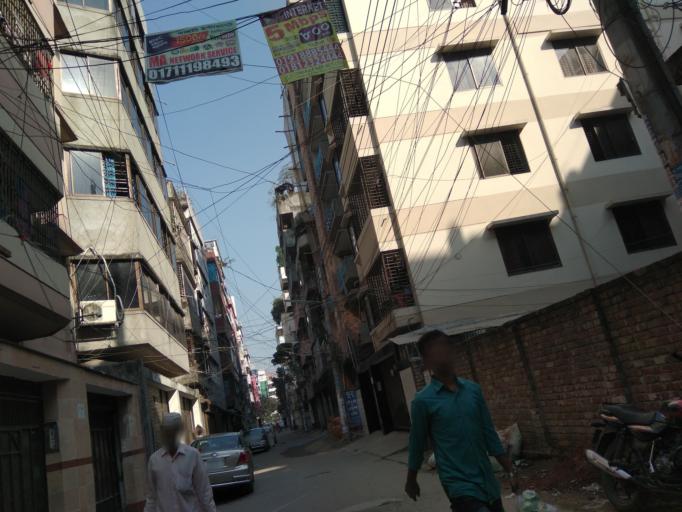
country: BD
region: Dhaka
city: Azimpur
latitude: 23.7729
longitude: 90.3637
